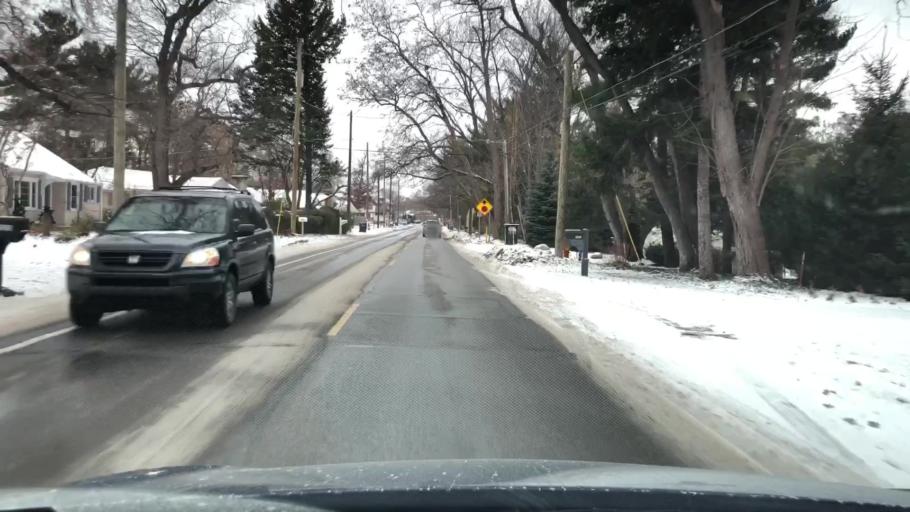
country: US
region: Michigan
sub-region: Grand Traverse County
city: Traverse City
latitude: 44.7653
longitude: -85.5977
